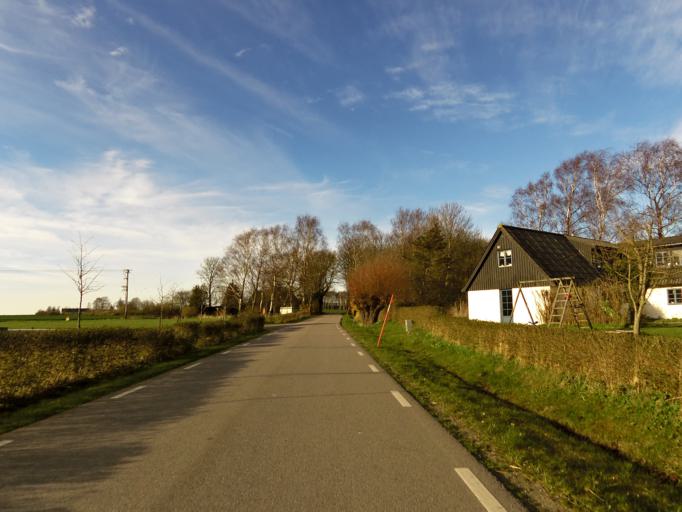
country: SE
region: Skane
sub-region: Kavlinge Kommun
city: Loddekopinge
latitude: 55.7507
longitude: 13.0645
